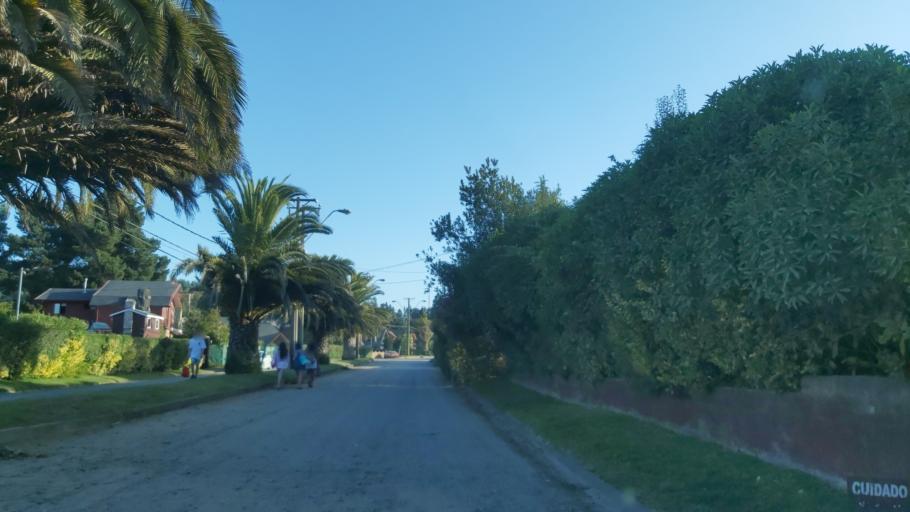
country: CL
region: Biobio
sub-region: Provincia de Concepcion
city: Tome
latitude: -36.5322
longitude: -72.9303
